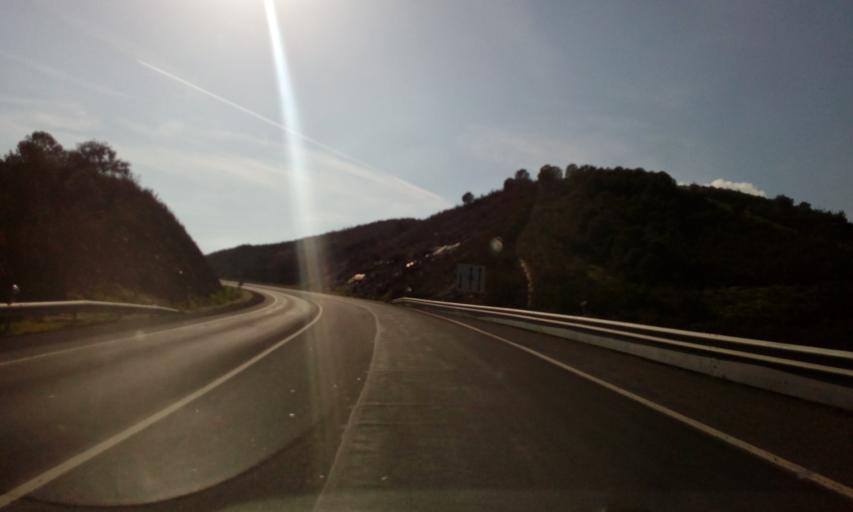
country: PT
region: Faro
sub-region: Castro Marim
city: Castro Marim
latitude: 37.2726
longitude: -7.4966
